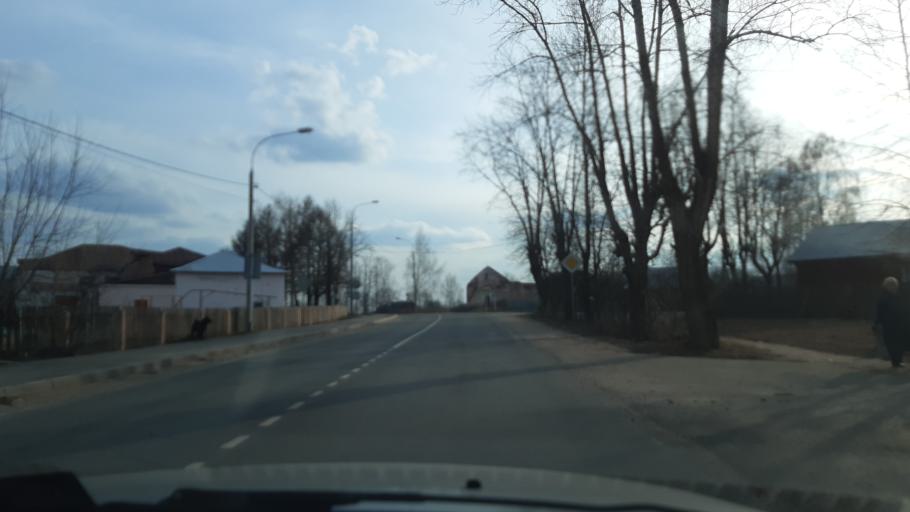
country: RU
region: Vladimir
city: Nikologory
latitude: 56.1477
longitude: 41.9938
